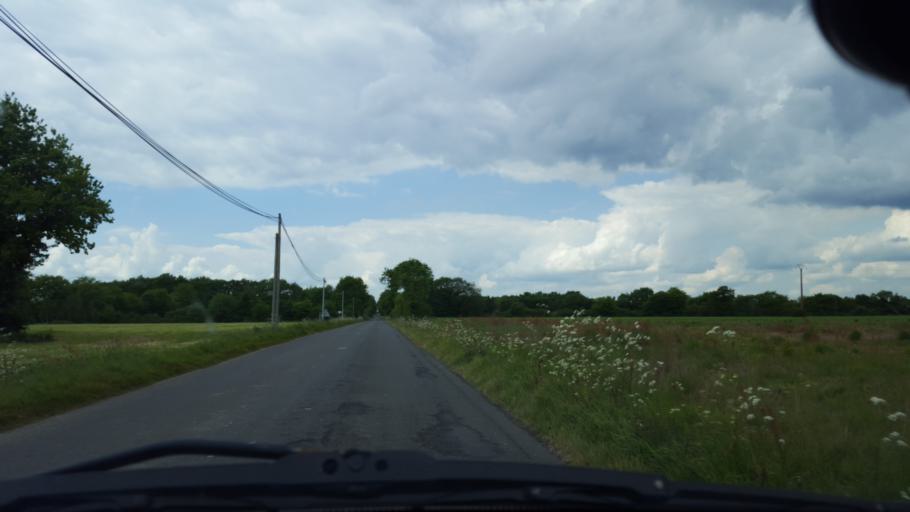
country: FR
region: Pays de la Loire
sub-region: Departement de la Loire-Atlantique
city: Saint-Philbert-de-Grand-Lieu
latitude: 47.0409
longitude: -1.6054
